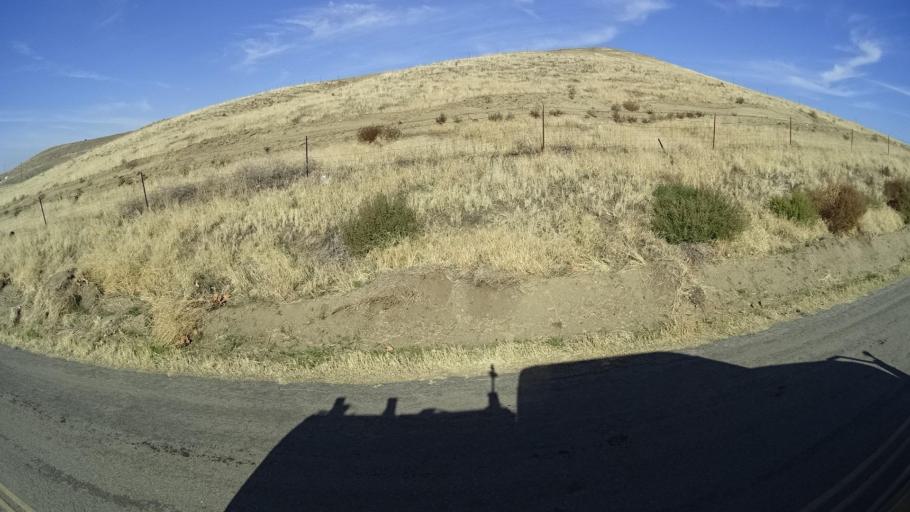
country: US
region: California
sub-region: Kern County
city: Lamont
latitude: 35.3869
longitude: -118.8194
